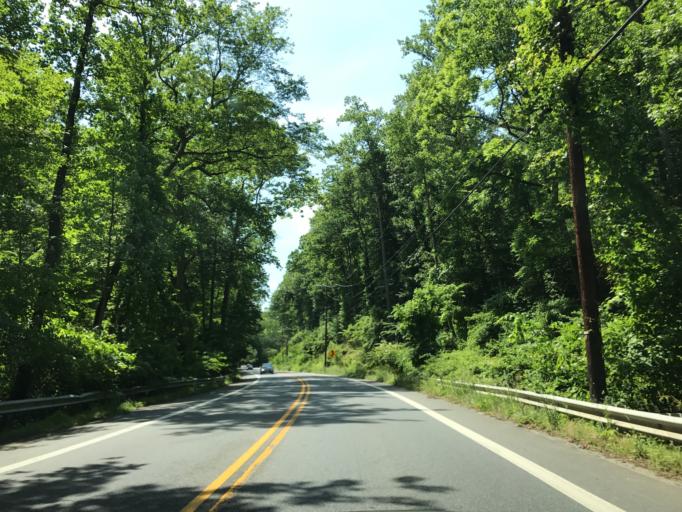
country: US
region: Maryland
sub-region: Anne Arundel County
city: Riva
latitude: 38.9884
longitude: -76.5729
